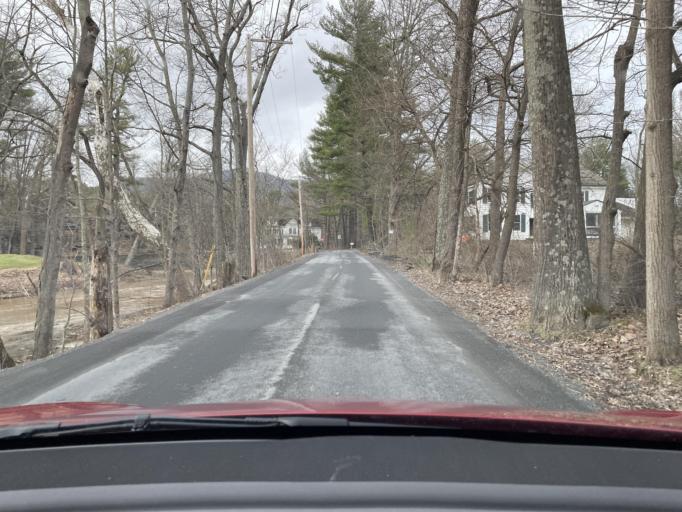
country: US
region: New York
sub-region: Ulster County
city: Woodstock
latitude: 42.0356
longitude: -74.1053
